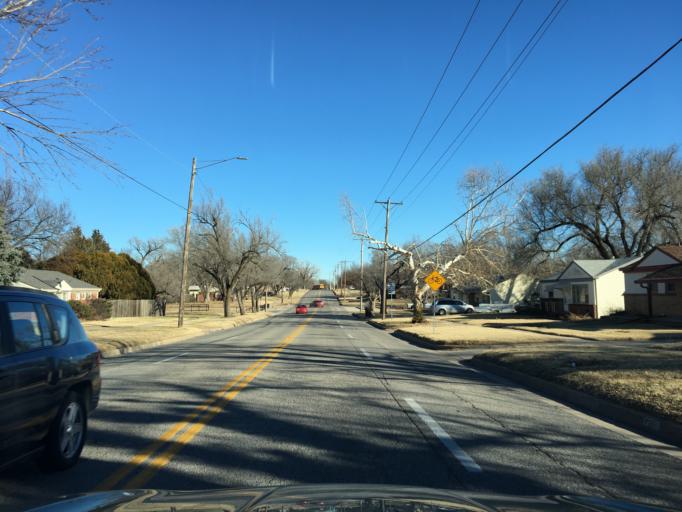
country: US
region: Kansas
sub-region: Sedgwick County
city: Wichita
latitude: 37.6719
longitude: -97.2515
